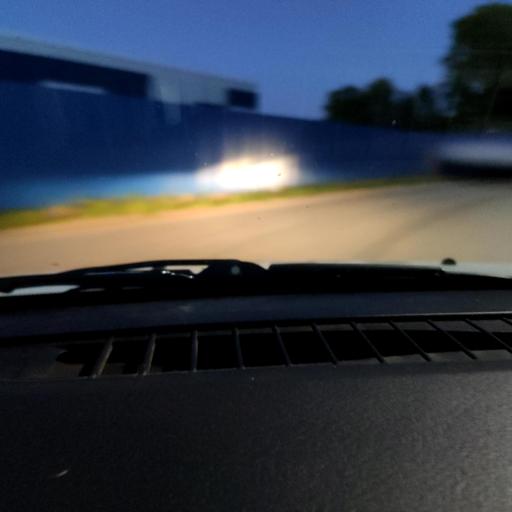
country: RU
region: Perm
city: Zvezdnyy
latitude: 57.7380
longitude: 56.3217
